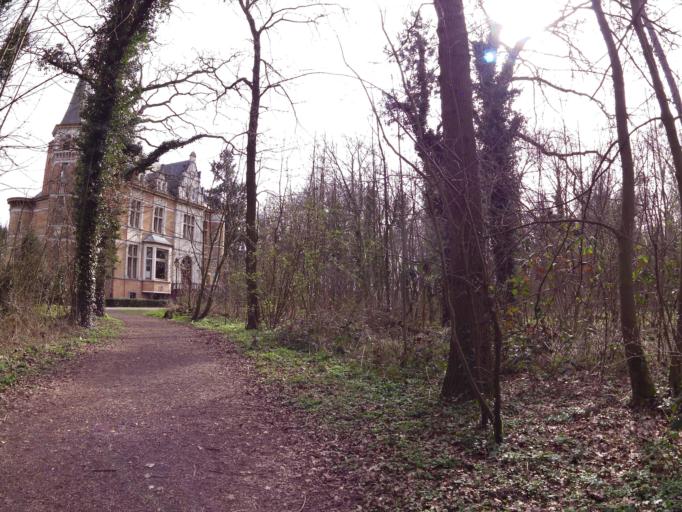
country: BE
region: Flanders
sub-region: Provincie West-Vlaanderen
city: Diksmuide
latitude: 50.9844
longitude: 2.8708
